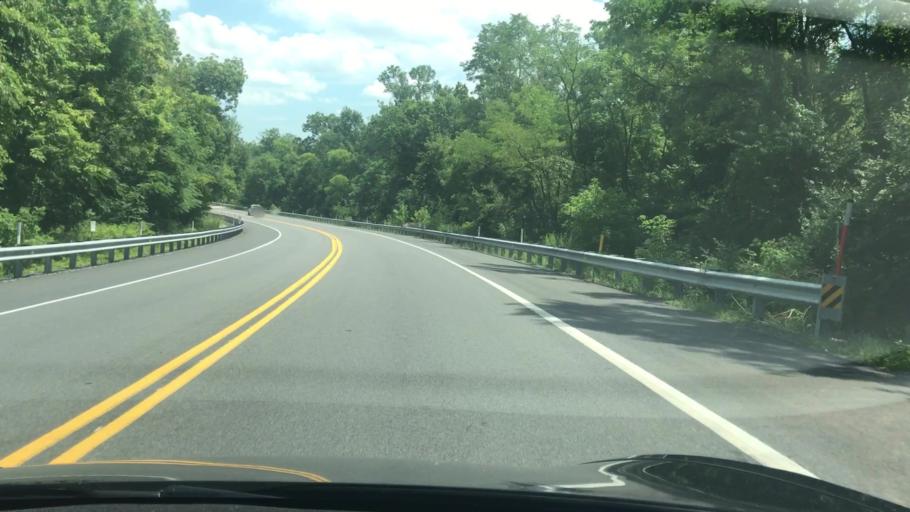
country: US
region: Pennsylvania
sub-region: York County
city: Valley Green
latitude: 40.1292
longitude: -76.8572
